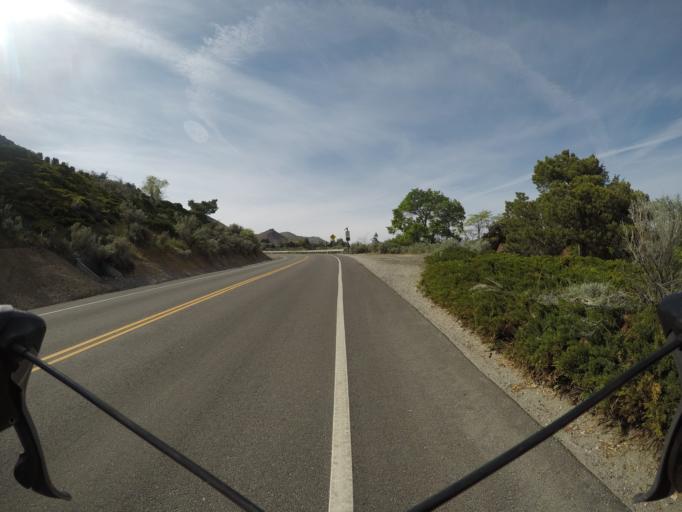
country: US
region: Washington
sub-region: Chelan County
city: Wenatchee
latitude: 47.4086
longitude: -120.3370
